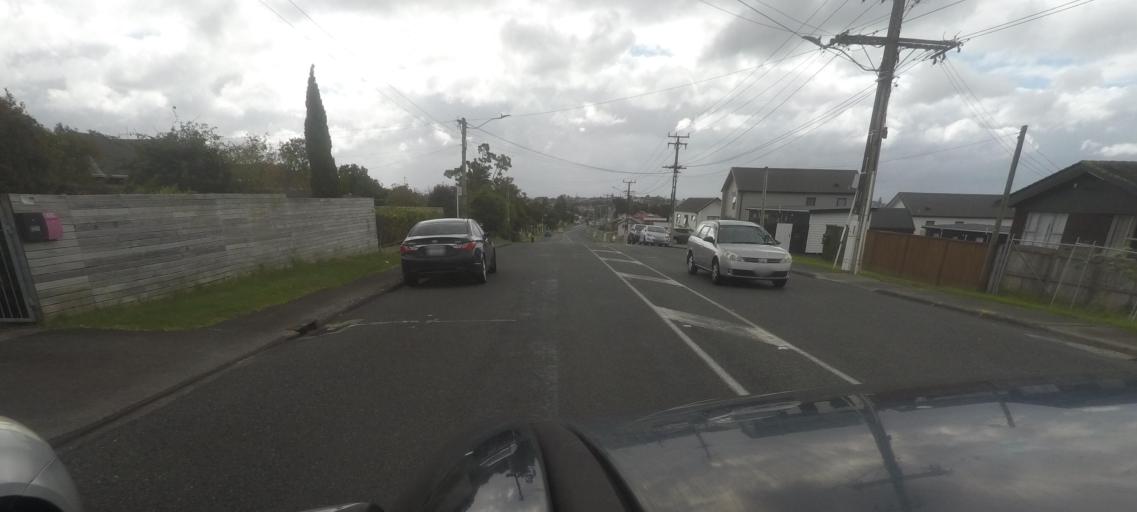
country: NZ
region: Auckland
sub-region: Auckland
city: Auckland
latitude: -36.9183
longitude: 174.7335
